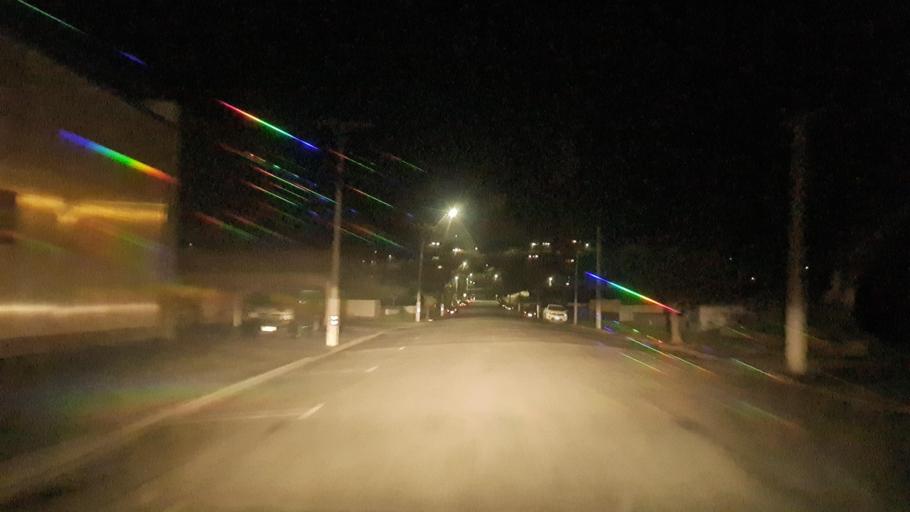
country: NZ
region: Otago
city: Oamaru
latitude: -45.0914
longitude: 170.9782
